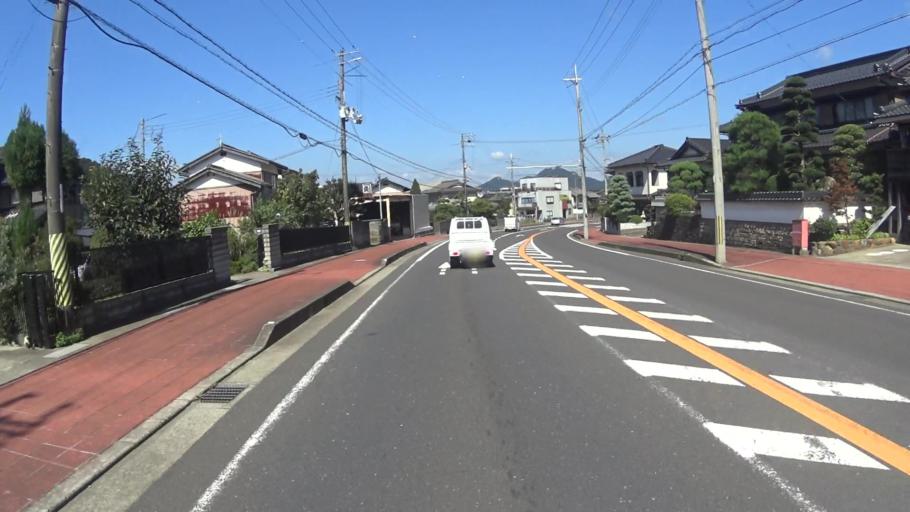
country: JP
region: Kyoto
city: Ayabe
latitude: 35.2940
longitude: 135.2676
